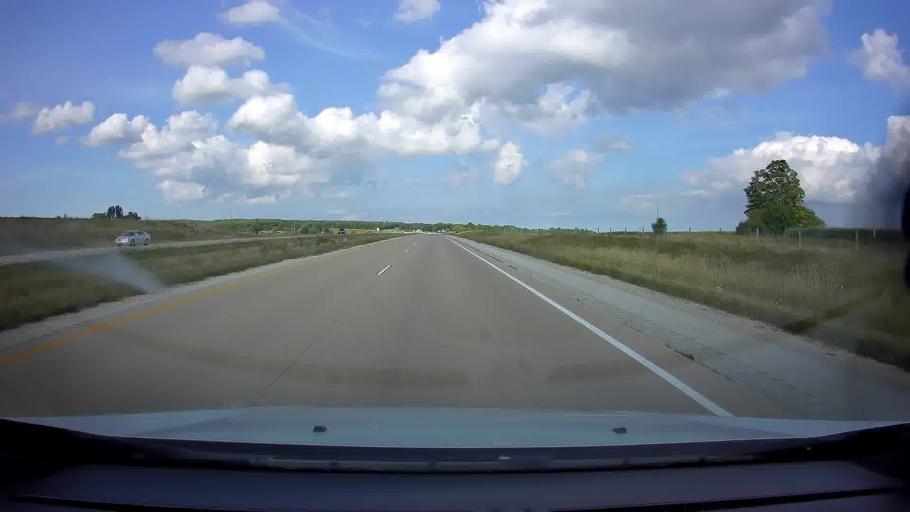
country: US
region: Wisconsin
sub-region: Kewaunee County
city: Algoma
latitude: 44.7302
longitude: -87.6005
